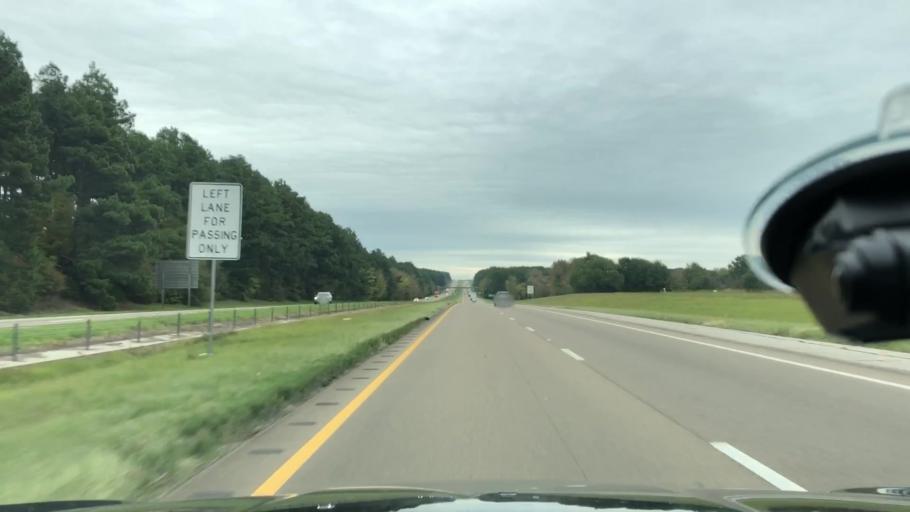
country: US
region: Texas
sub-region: Titus County
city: Mount Pleasant
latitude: 33.1842
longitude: -94.9539
